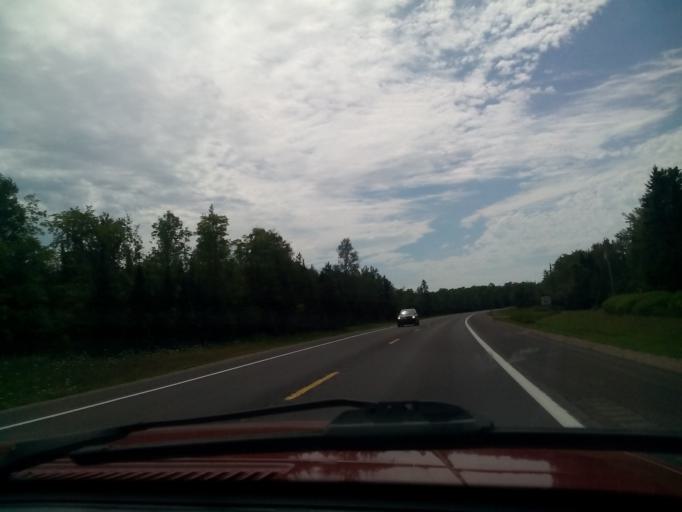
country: US
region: Michigan
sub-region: Schoolcraft County
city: Manistique
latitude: 46.0613
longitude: -85.9587
